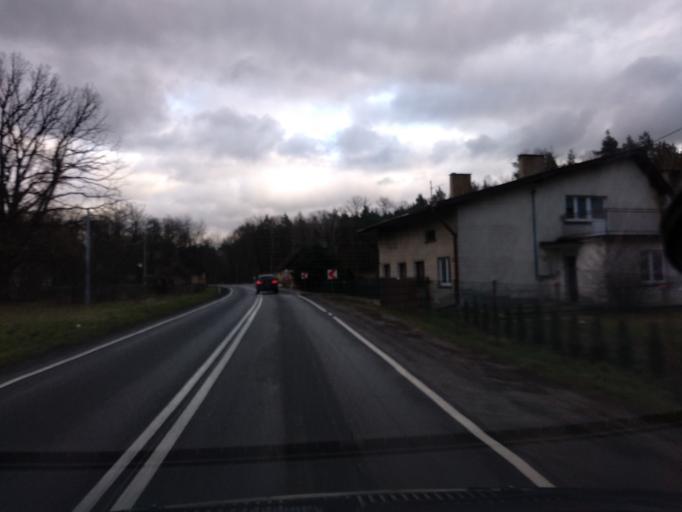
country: PL
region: Lower Silesian Voivodeship
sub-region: Powiat olesnicki
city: Miedzyborz
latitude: 51.4658
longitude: 17.7348
